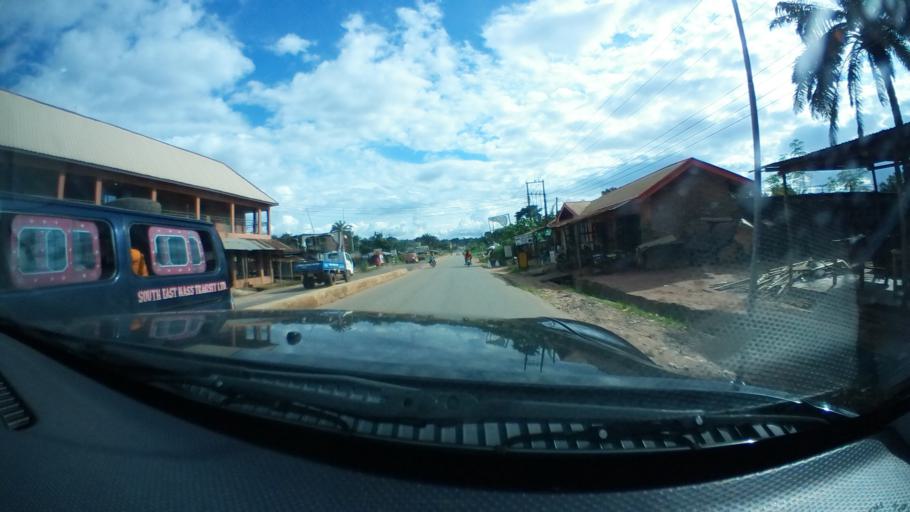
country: NG
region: Anambra
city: Uga
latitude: 5.9036
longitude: 7.1090
